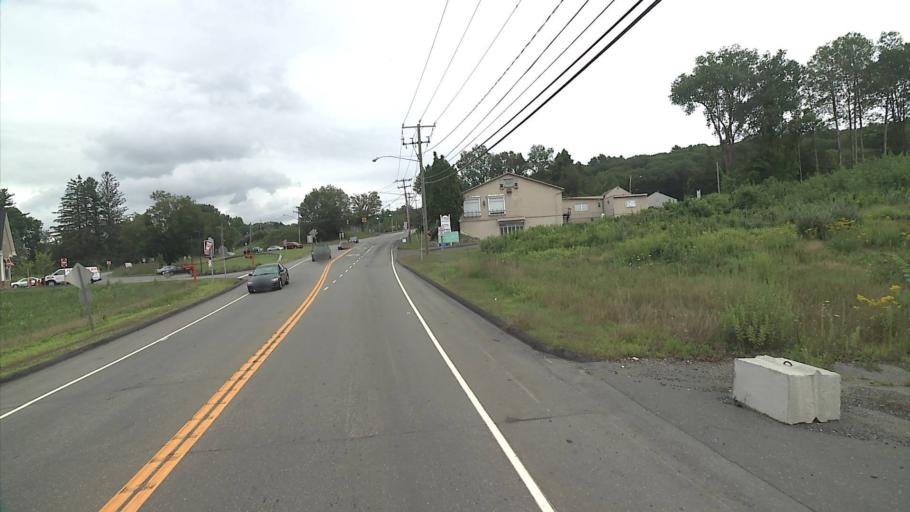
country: US
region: Connecticut
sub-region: Tolland County
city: Tolland
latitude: 41.8809
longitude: -72.3030
